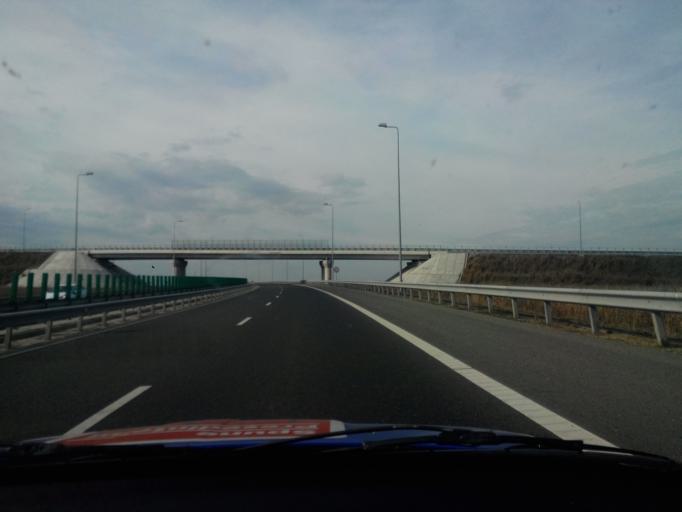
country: RO
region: Constanta
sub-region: Comuna Cumpana
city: Cumpana
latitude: 44.1448
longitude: 28.5553
